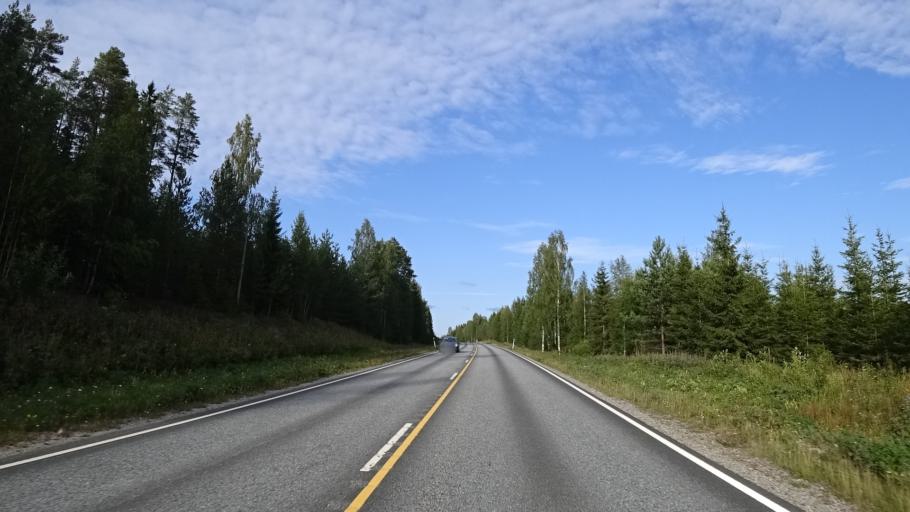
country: FI
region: North Karelia
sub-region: Joensuu
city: Eno
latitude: 62.8120
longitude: 30.1717
